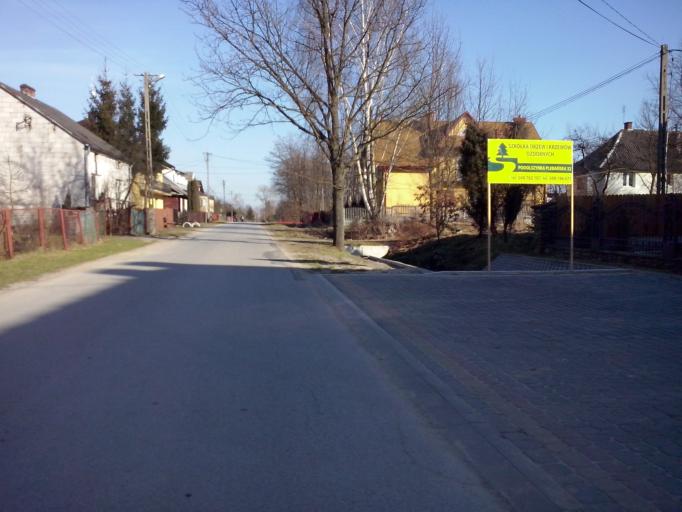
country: PL
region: Subcarpathian Voivodeship
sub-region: Powiat nizanski
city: Krzeszow
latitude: 50.4144
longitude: 22.3756
